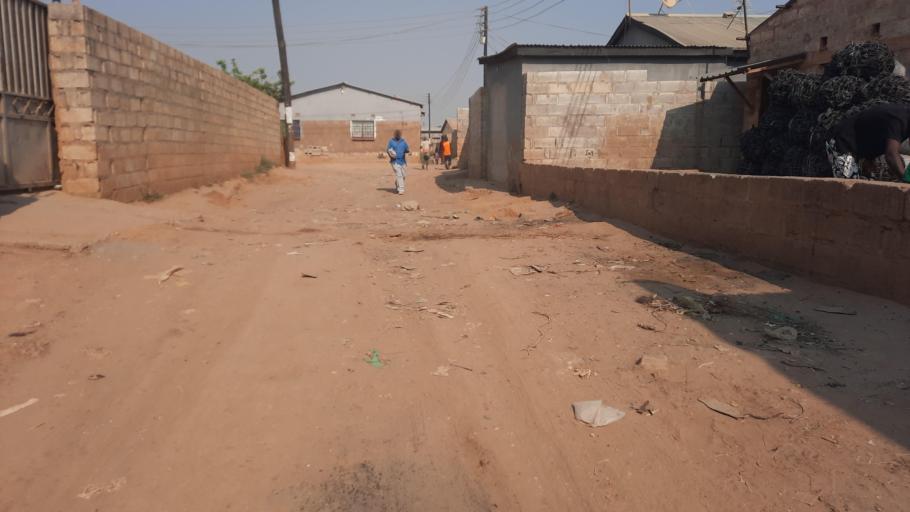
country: ZM
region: Lusaka
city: Lusaka
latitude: -15.3976
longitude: 28.3822
